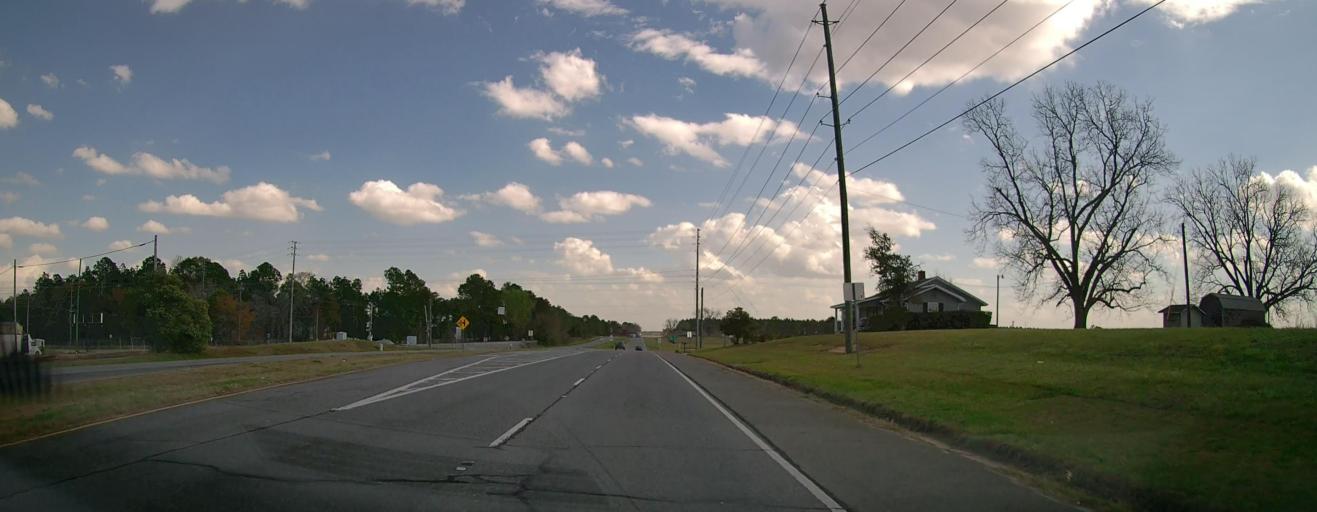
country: US
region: Georgia
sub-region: Dodge County
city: Eastman
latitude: 32.1704
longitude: -83.1572
